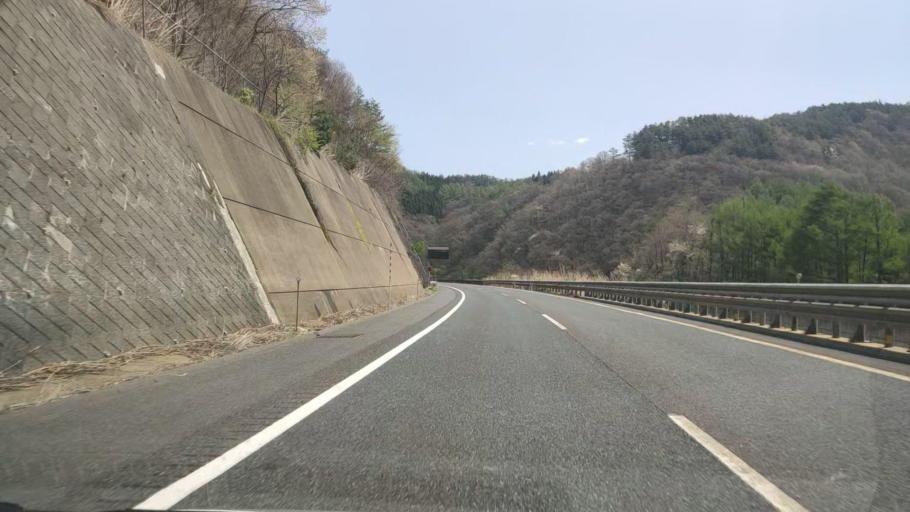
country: JP
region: Iwate
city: Ichinohe
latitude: 40.2229
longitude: 141.2572
